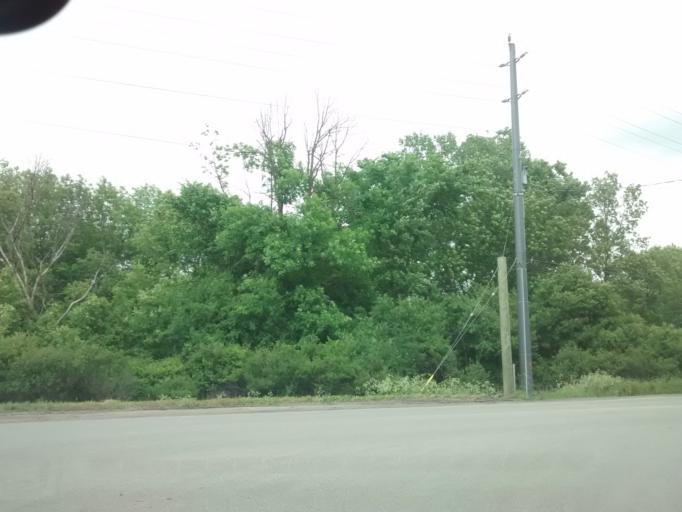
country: CA
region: Ontario
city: Brockville
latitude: 44.6519
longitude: -75.6253
